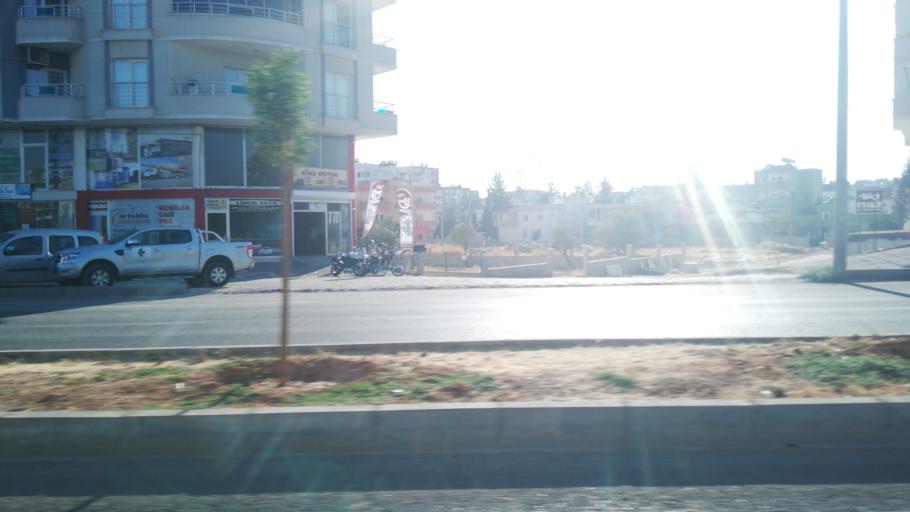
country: TR
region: Mardin
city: Midyat
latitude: 37.4249
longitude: 41.3458
